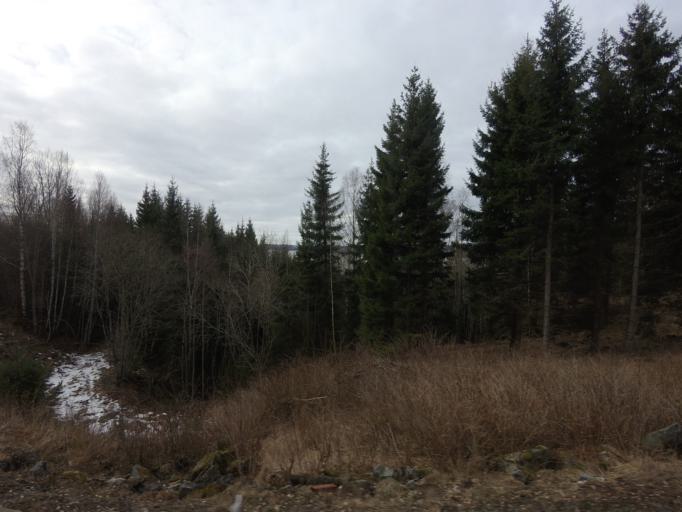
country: NO
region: Akershus
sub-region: Enebakk
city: Flateby
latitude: 59.8181
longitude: 11.2451
